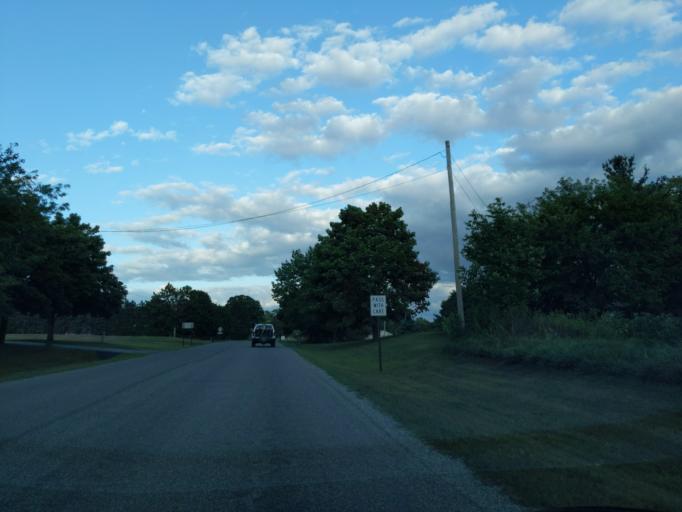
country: US
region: Michigan
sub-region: Ingham County
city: Holt
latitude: 42.5968
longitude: -84.5815
